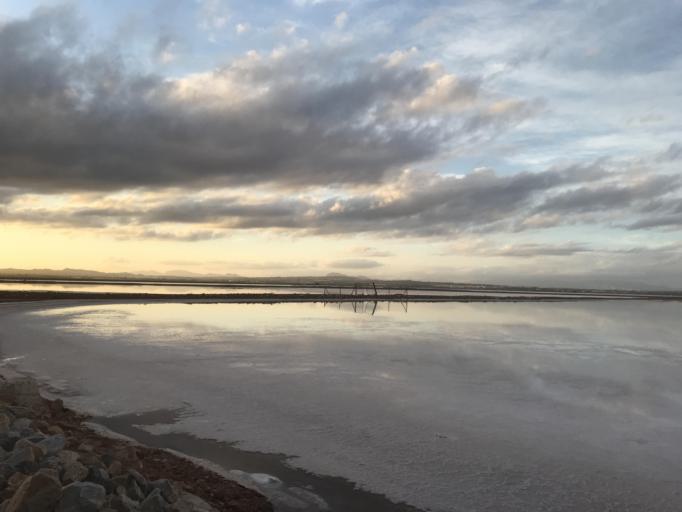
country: ES
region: Valencia
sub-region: Provincia de Alicante
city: Torrevieja
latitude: 37.9806
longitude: -0.7041
